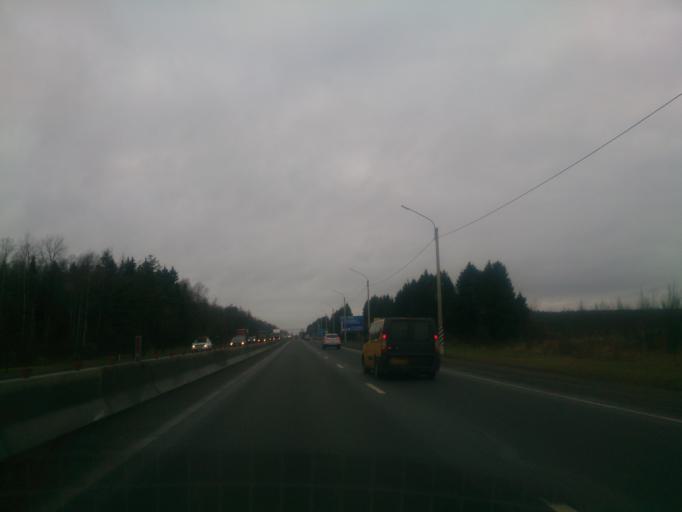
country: RU
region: Leningrad
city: Ul'yanovka
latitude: 59.6239
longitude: 30.7260
